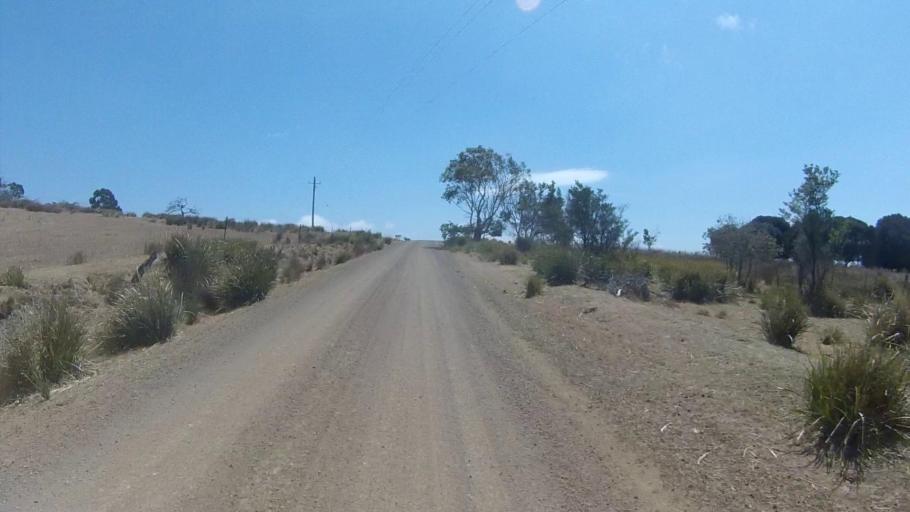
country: AU
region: Tasmania
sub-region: Sorell
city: Sorell
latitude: -42.8958
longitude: 147.8646
